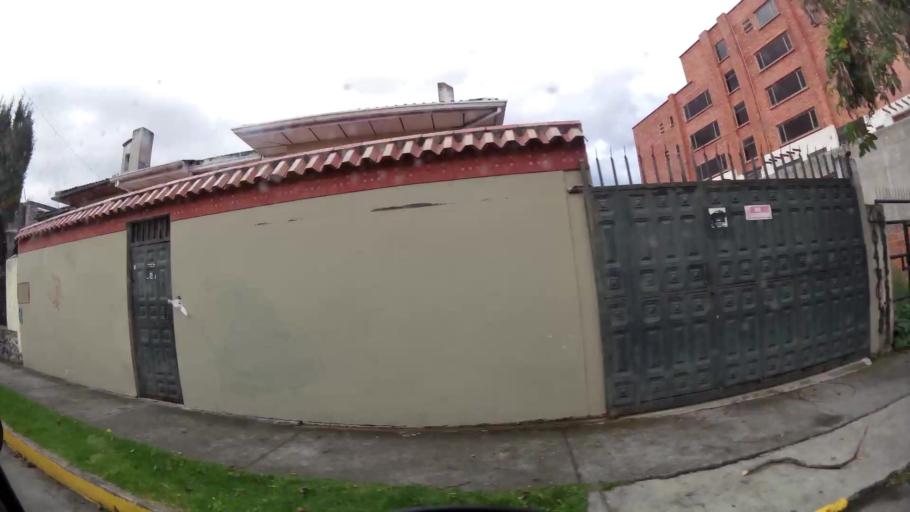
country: EC
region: Azuay
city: Cuenca
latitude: -2.8987
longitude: -79.0225
